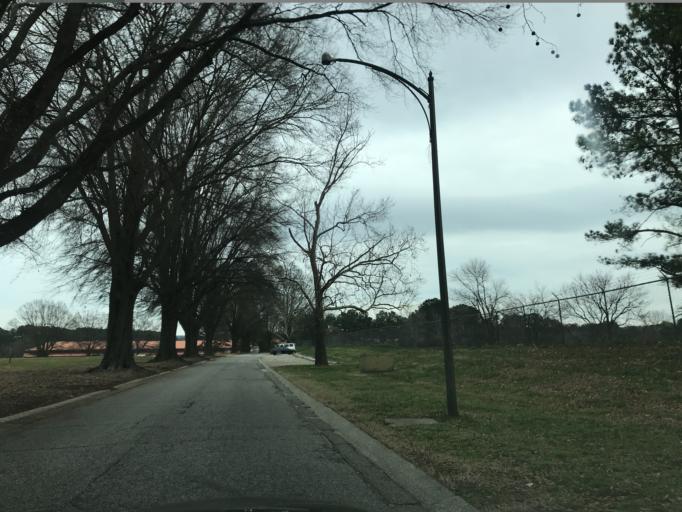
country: US
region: North Carolina
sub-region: Wake County
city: West Raleigh
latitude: 35.7677
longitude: -78.6639
